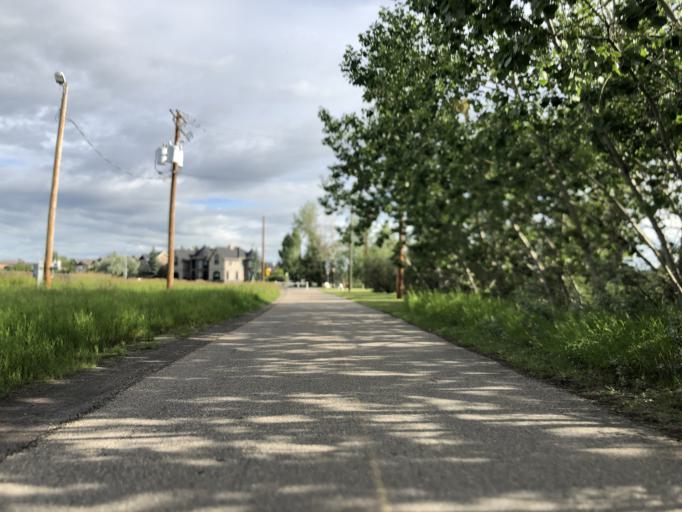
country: CA
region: Alberta
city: Calgary
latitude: 51.0306
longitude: -114.0113
